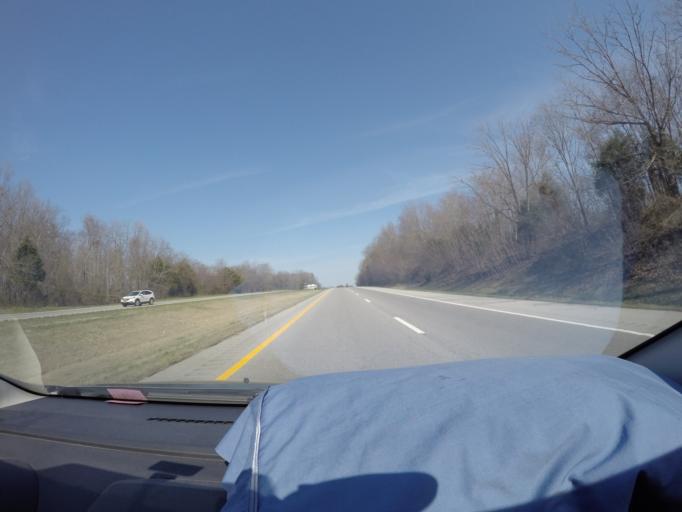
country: US
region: Tennessee
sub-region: Franklin County
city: Sewanee
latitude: 35.3350
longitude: -85.9357
